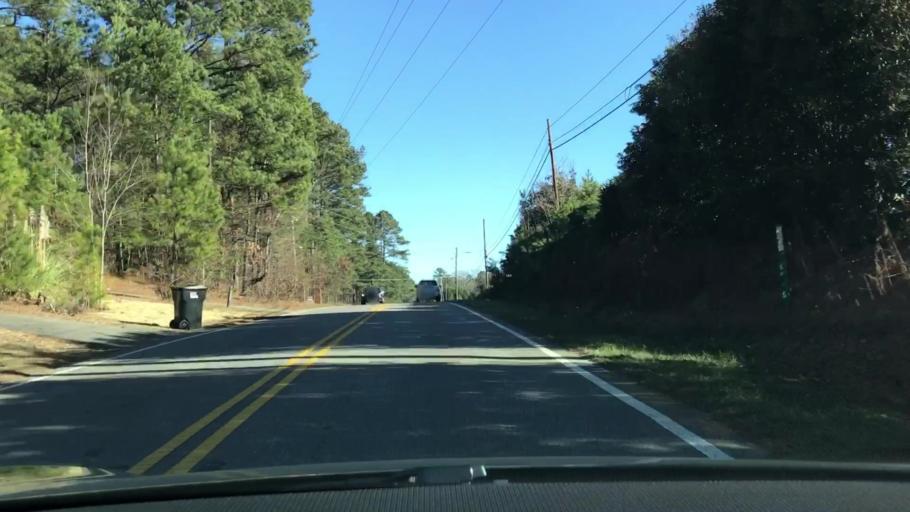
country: US
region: Georgia
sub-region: Forsyth County
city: Cumming
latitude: 34.1824
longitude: -84.0976
